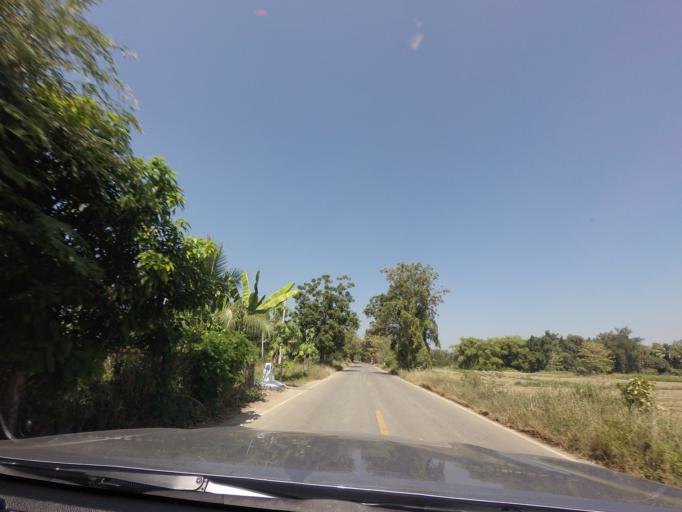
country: TH
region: Sukhothai
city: Si Samrong
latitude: 17.1409
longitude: 99.7707
